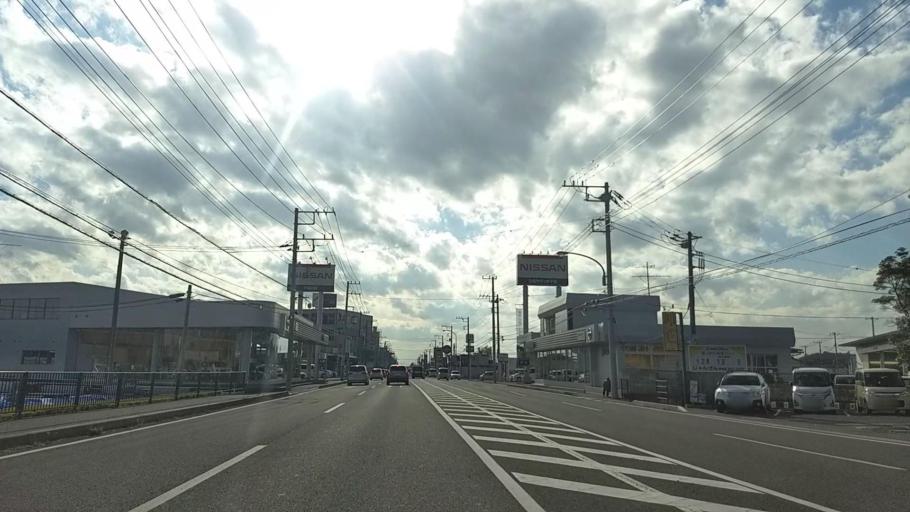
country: JP
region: Chiba
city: Togane
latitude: 35.5741
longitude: 140.3803
